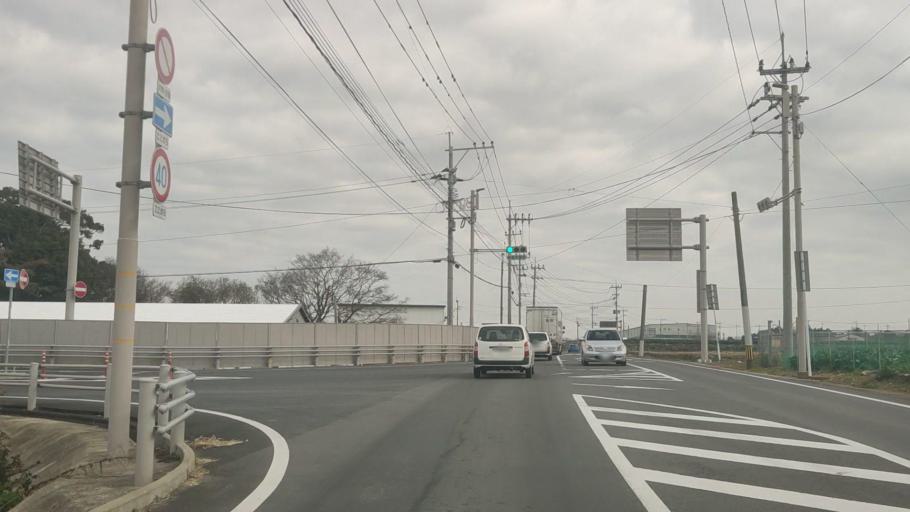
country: JP
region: Nagasaki
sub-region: Isahaya-shi
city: Isahaya
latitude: 32.8175
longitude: 130.1760
